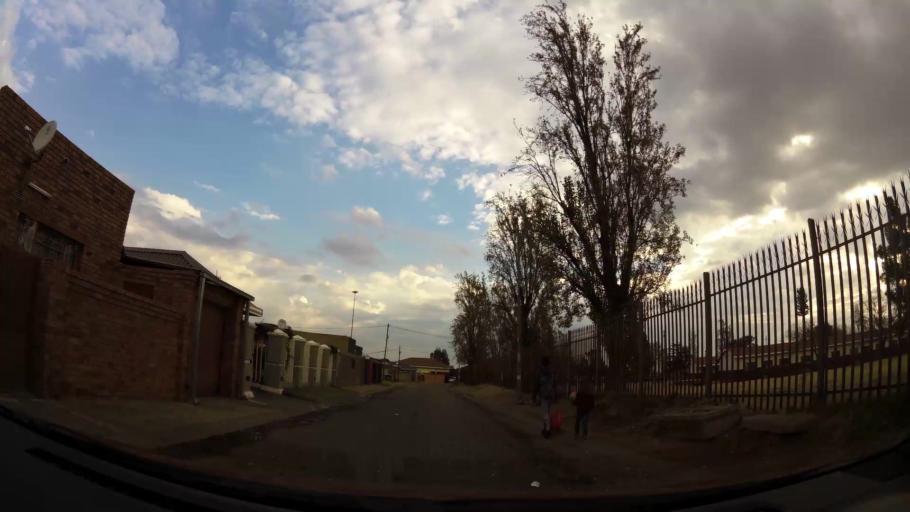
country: ZA
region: Gauteng
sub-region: City of Johannesburg Metropolitan Municipality
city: Soweto
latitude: -26.2419
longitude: 27.8256
